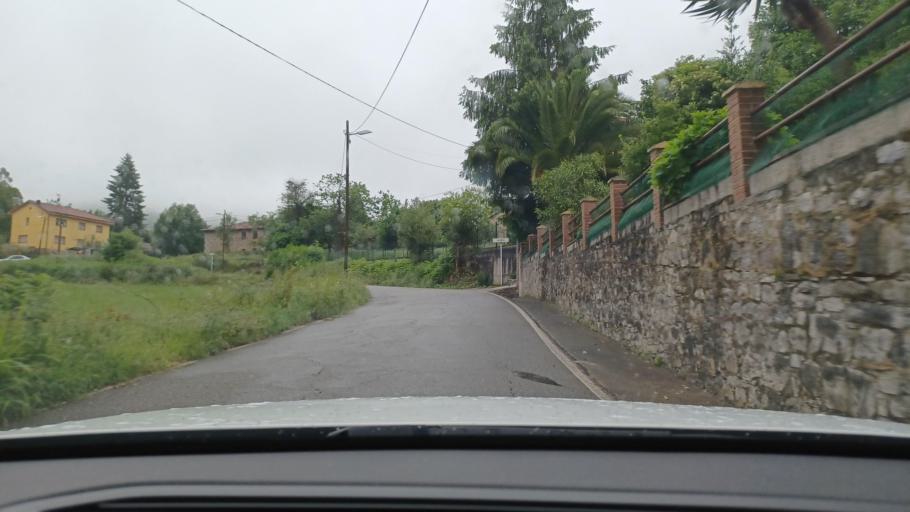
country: ES
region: Asturias
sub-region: Province of Asturias
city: Castandiello
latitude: 43.3035
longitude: -5.9344
